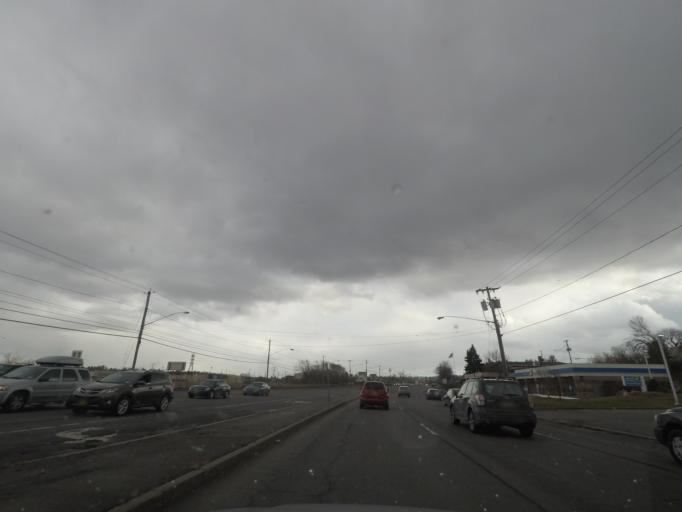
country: US
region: New York
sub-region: Onondaga County
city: East Syracuse
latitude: 43.0492
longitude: -76.0710
